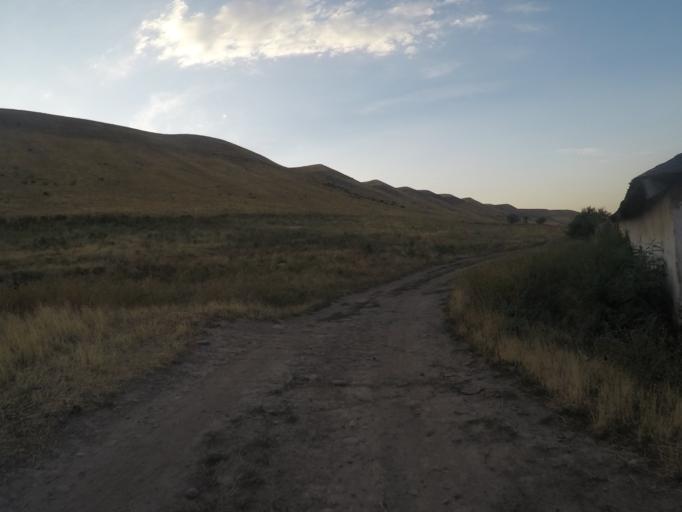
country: KG
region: Chuy
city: Bishkek
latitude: 42.7655
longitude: 74.6380
